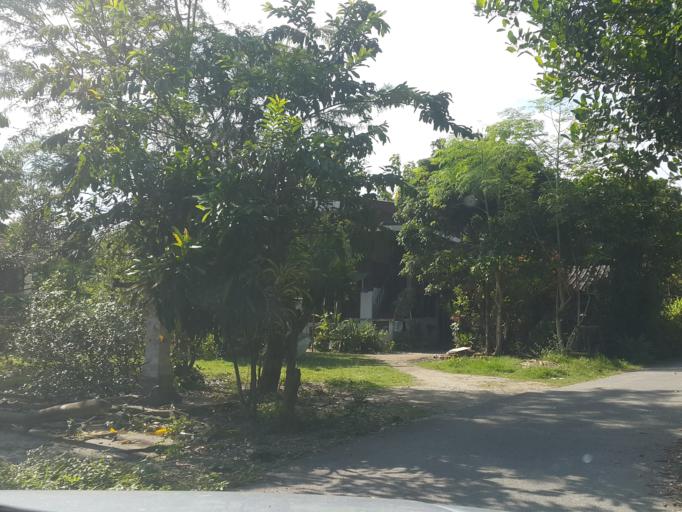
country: TH
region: Chiang Mai
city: Saraphi
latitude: 18.7329
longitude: 99.0441
